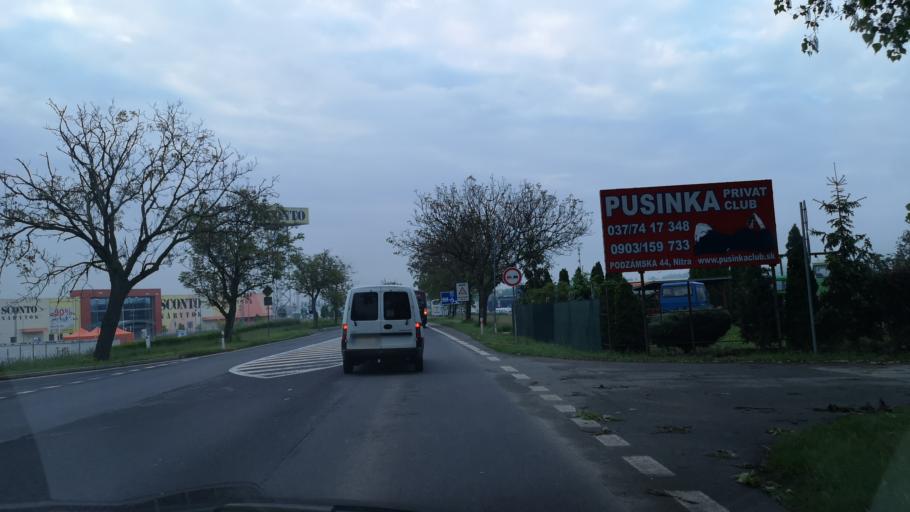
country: SK
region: Nitriansky
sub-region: Okres Nitra
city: Nitra
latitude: 48.3246
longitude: 18.0321
